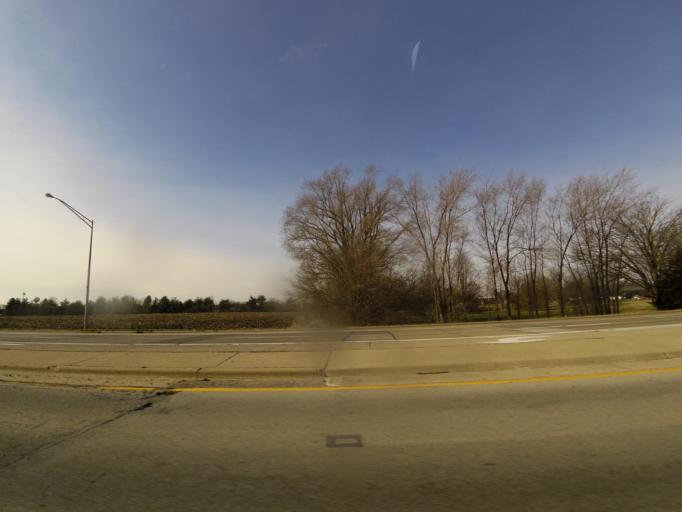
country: US
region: Illinois
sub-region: Macon County
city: Forsyth
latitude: 39.9270
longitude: -88.9555
